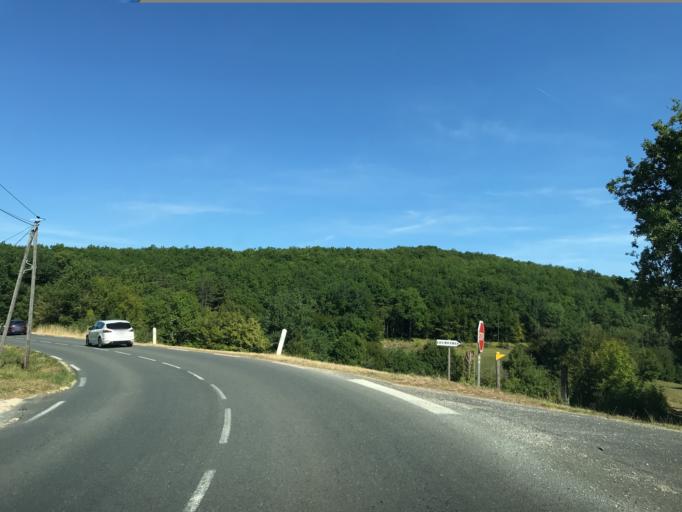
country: FR
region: Limousin
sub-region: Departement de la Correze
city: Larche
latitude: 45.0809
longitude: 1.3777
